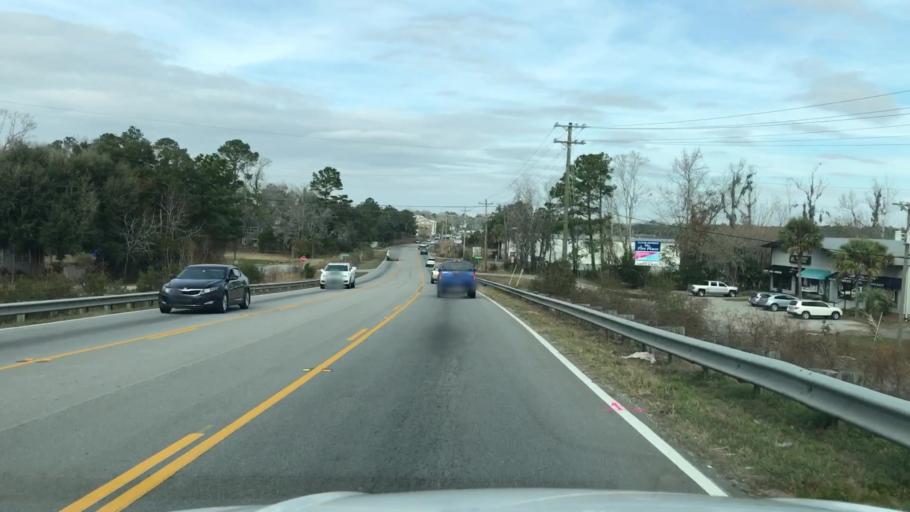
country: US
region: South Carolina
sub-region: Charleston County
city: Shell Point
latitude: 32.7942
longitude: -80.1080
